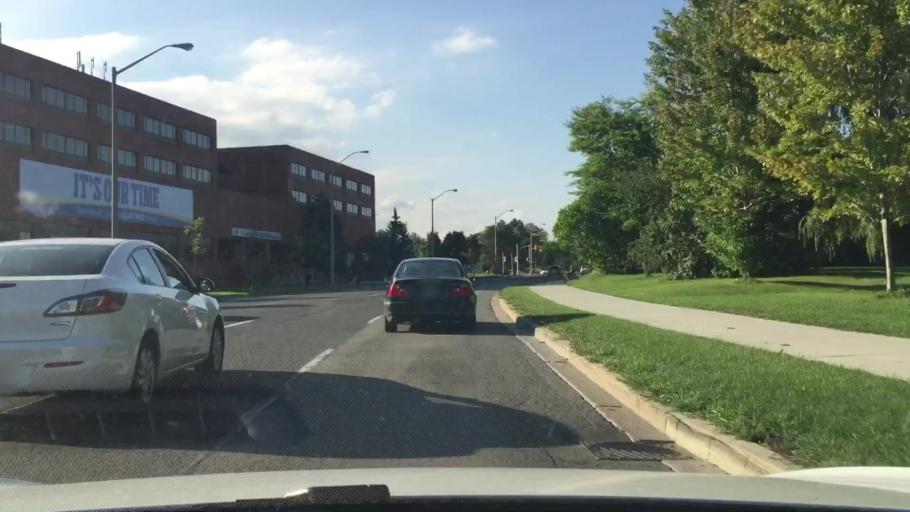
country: CA
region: Ontario
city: Scarborough
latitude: 43.8013
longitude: -79.3076
